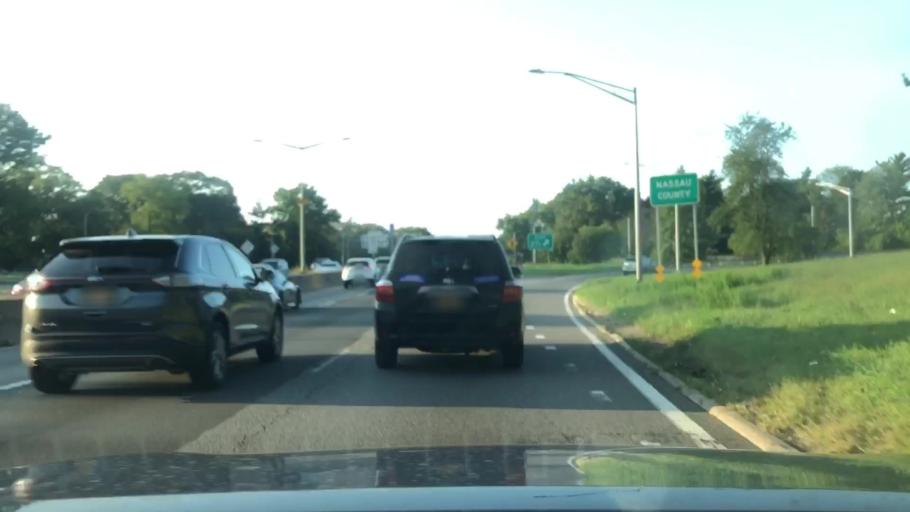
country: US
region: New York
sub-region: Nassau County
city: Bellerose Terrace
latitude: 40.7240
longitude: -73.7248
